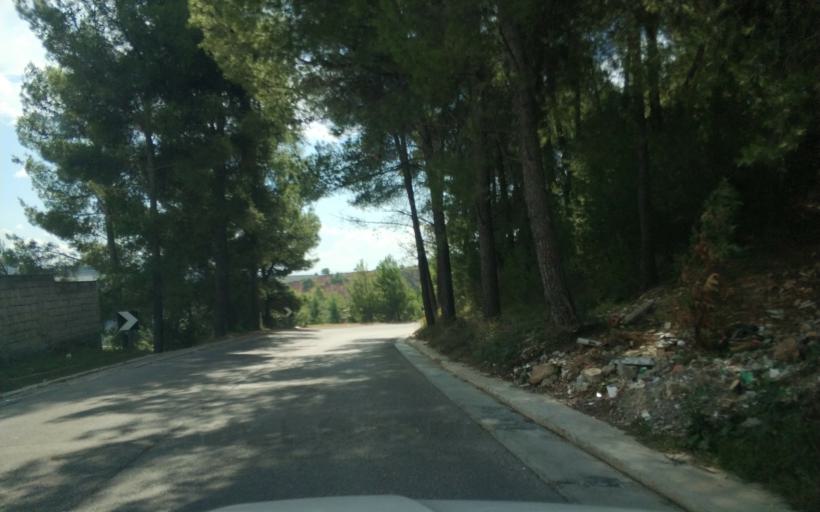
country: AL
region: Durres
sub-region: Rrethi i Krujes
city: Kruje
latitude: 41.4991
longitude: 19.7771
